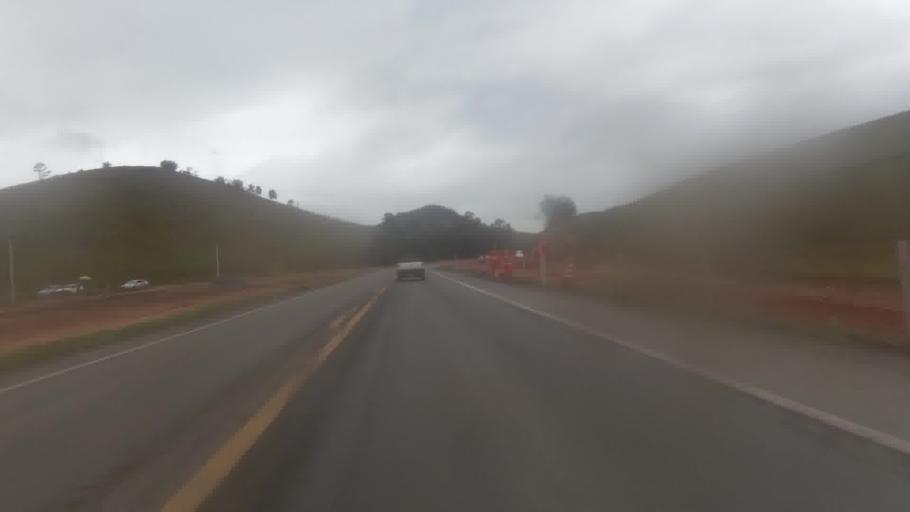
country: BR
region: Espirito Santo
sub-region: Alfredo Chaves
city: Alfredo Chaves
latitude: -20.7256
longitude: -40.7405
